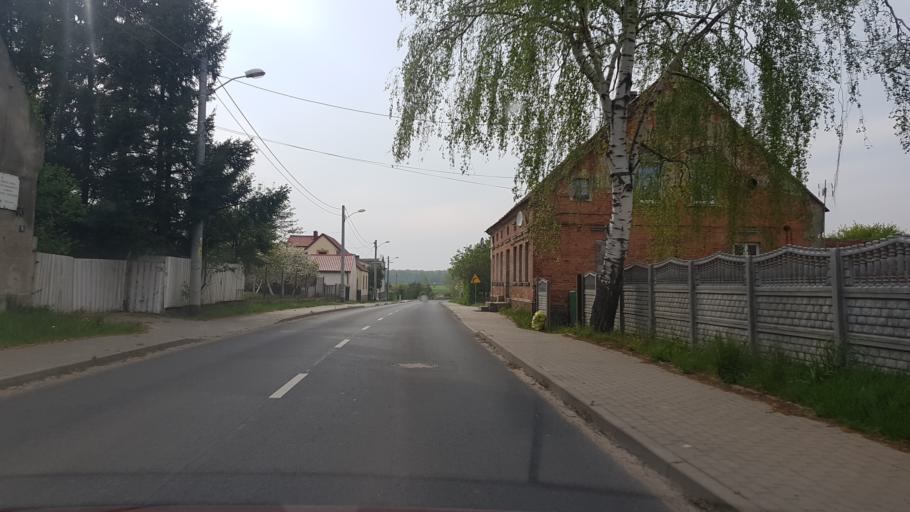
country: PL
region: West Pomeranian Voivodeship
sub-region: Powiat gryfinski
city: Stare Czarnowo
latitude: 53.2788
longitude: 14.7759
